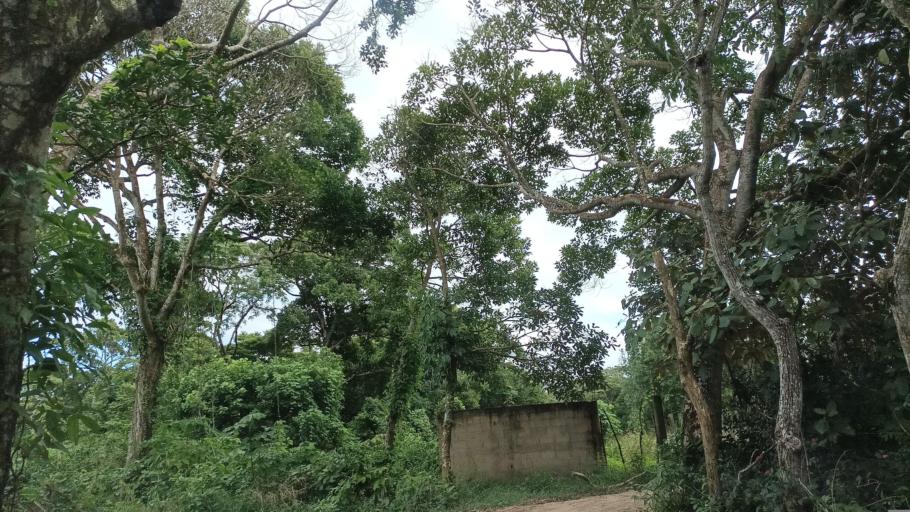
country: MX
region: Veracruz
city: Minatitlan
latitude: 18.0433
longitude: -94.5579
